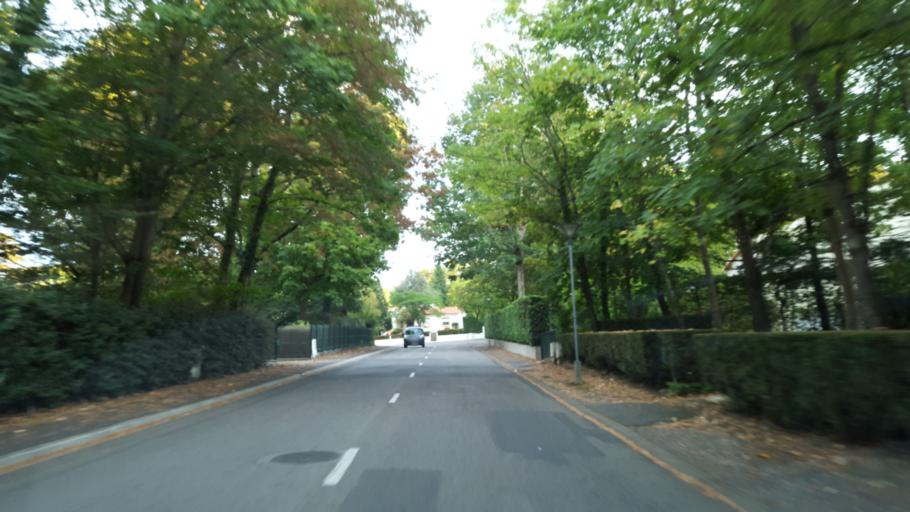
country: FR
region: Pays de la Loire
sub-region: Departement de la Loire-Atlantique
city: Basse-Goulaine
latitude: 47.2136
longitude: -1.4783
